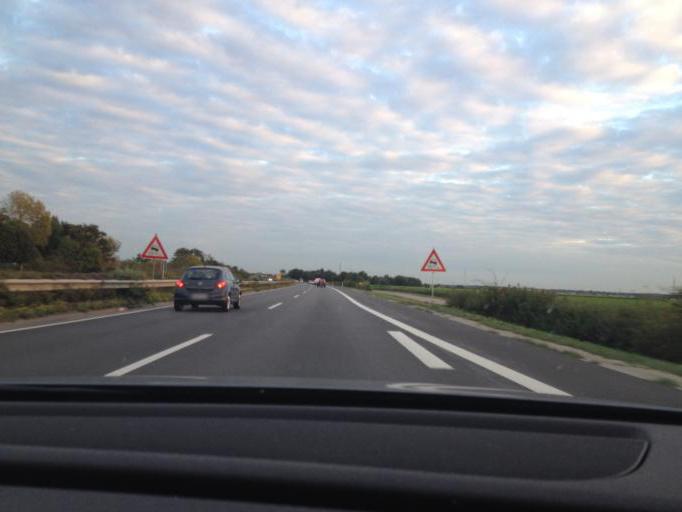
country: DE
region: Rheinland-Pfalz
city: Mutterstadt
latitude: 49.4473
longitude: 8.3696
